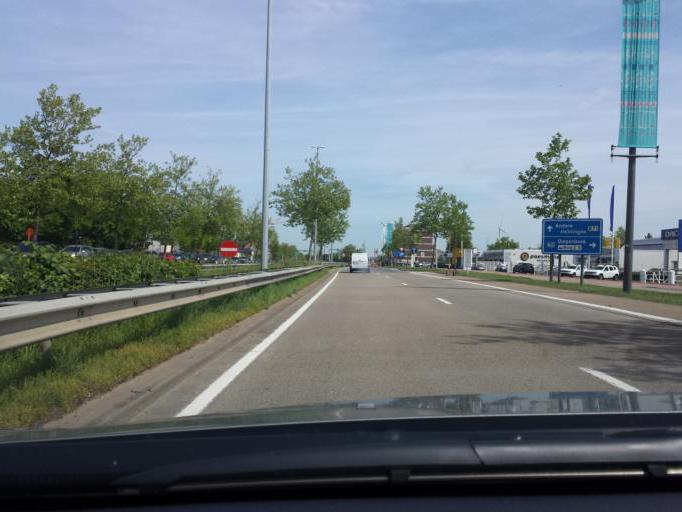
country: BE
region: Flanders
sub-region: Provincie Limburg
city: Hasselt
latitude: 50.9249
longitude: 5.3580
